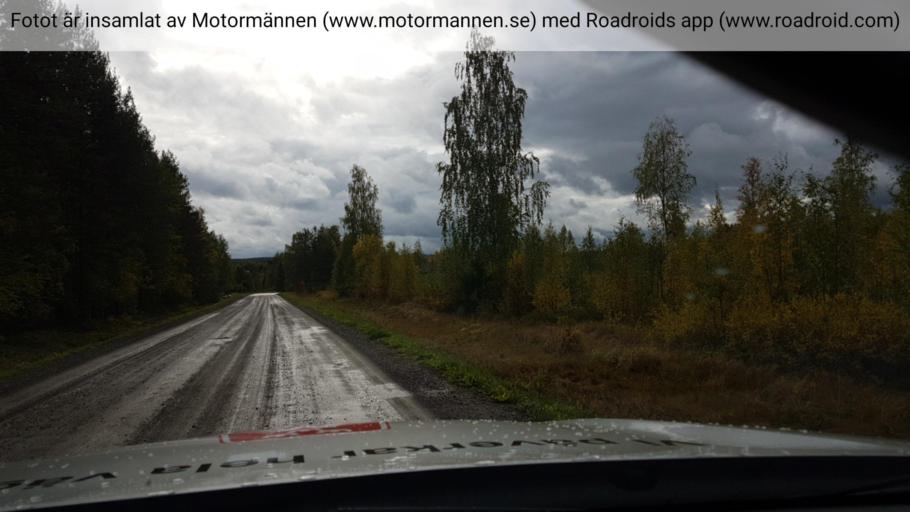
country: SE
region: Norrbotten
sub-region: Alvsbyns Kommun
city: AElvsbyn
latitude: 66.0909
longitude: 20.8924
